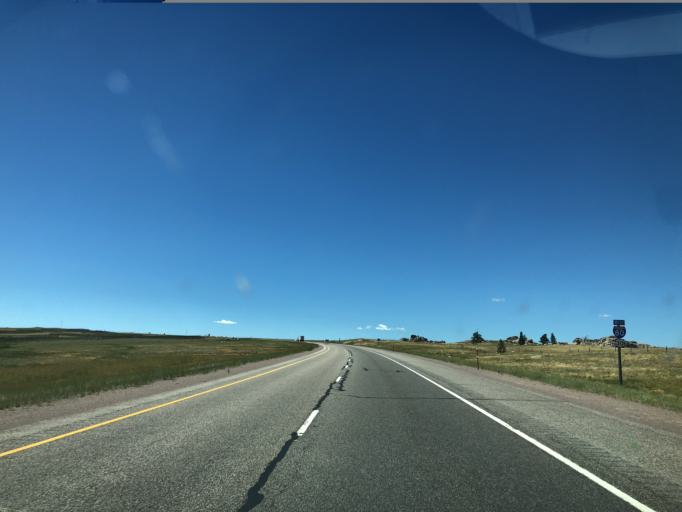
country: US
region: Wyoming
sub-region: Albany County
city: Laramie
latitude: 41.1401
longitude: -105.3545
